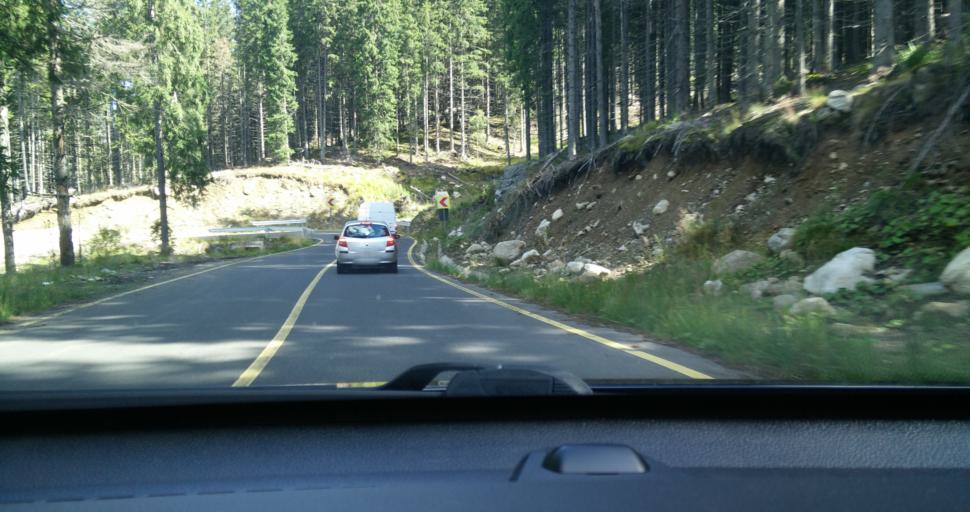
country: RO
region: Gorj
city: Novaci-Straini
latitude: 45.3922
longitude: 23.6327
